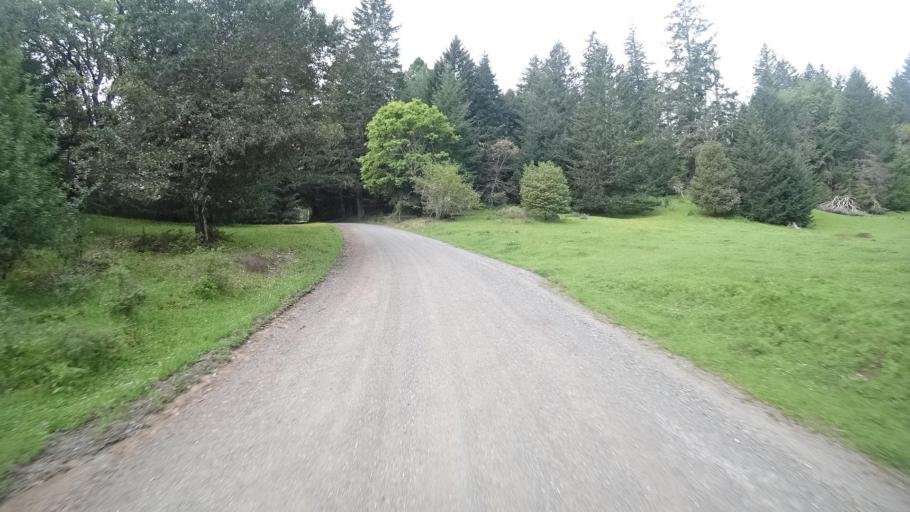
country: US
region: California
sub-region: Humboldt County
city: Redway
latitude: 40.2105
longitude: -123.6817
